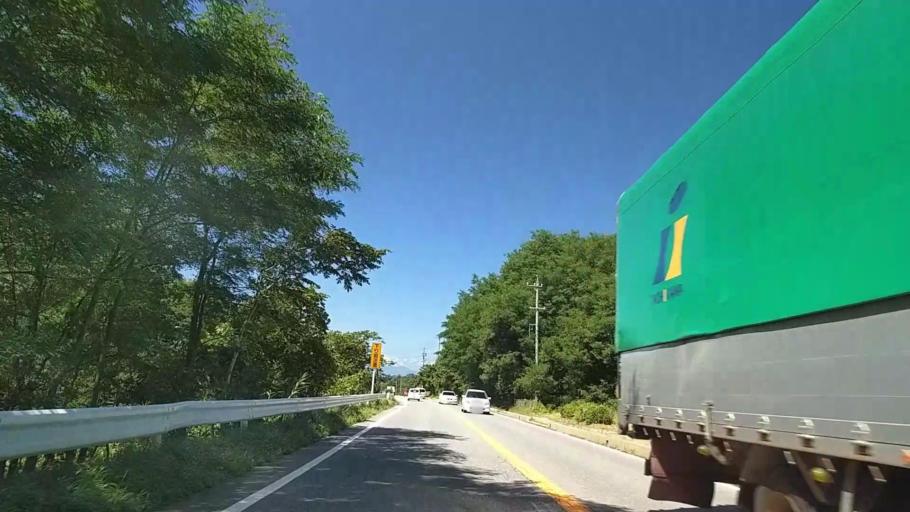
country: JP
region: Nagano
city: Komoro
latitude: 36.3502
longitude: 138.4195
